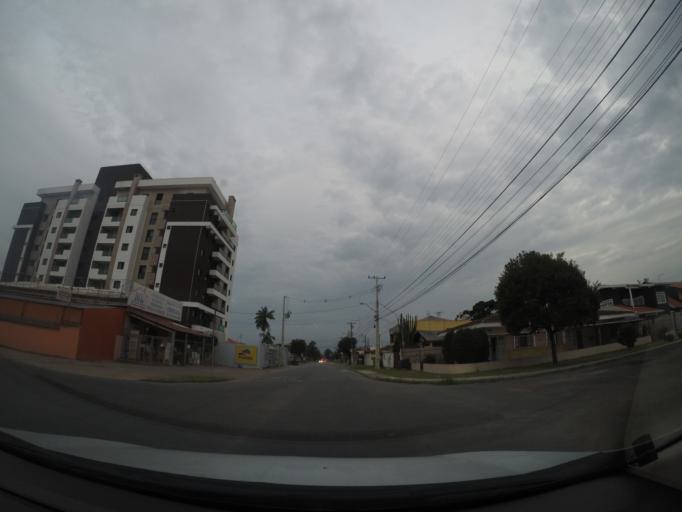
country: BR
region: Parana
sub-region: Sao Jose Dos Pinhais
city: Sao Jose dos Pinhais
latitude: -25.5126
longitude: -49.2334
